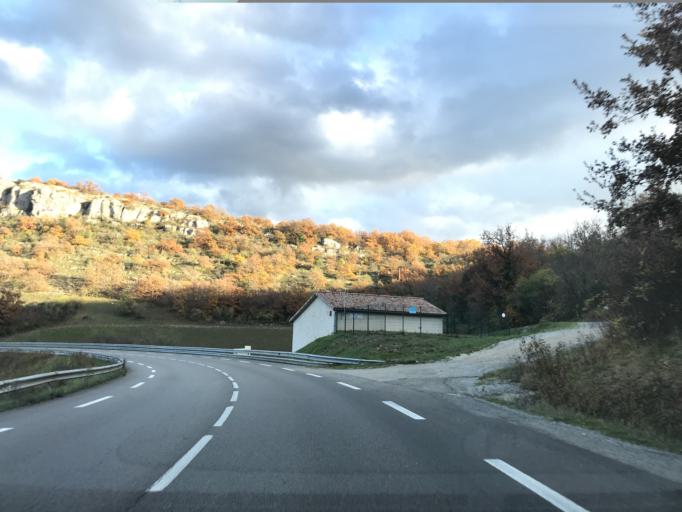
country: FR
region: Rhone-Alpes
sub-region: Departement de l'Ardeche
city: Alissas
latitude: 44.7101
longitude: 4.6231
